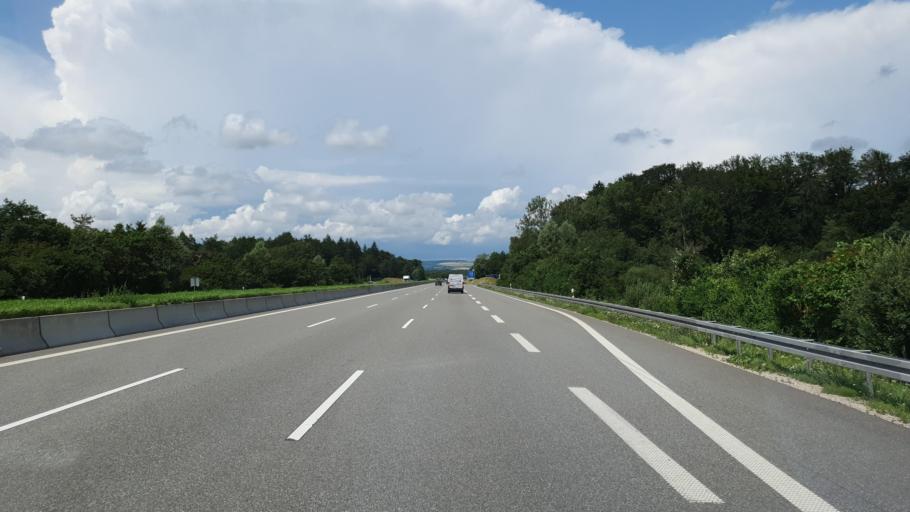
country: DE
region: Baden-Wuerttemberg
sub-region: Freiburg Region
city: Aach
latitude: 47.8225
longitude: 8.8377
